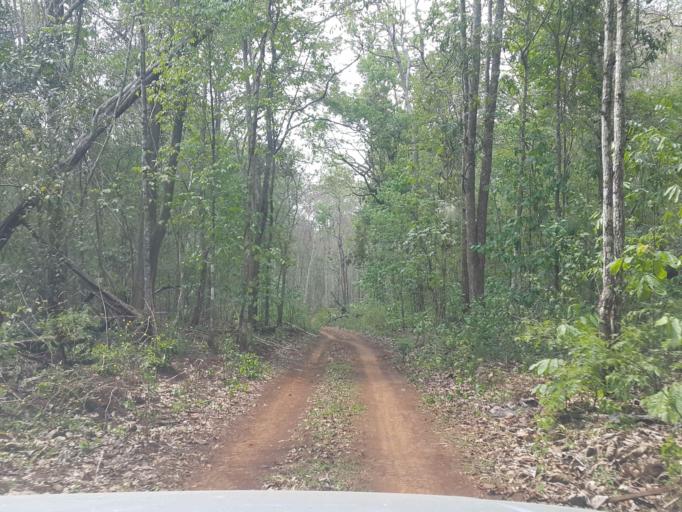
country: TH
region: Chiang Mai
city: Wiang Haeng
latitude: 19.3330
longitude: 98.7190
